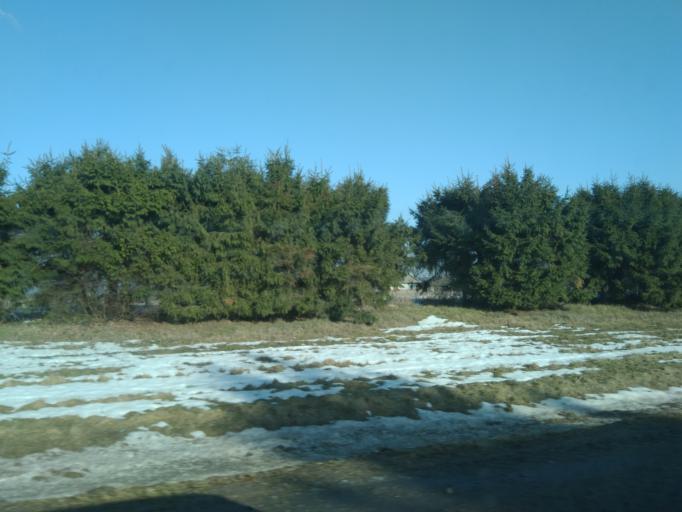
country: BY
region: Minsk
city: Snow
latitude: 53.2023
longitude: 26.4980
